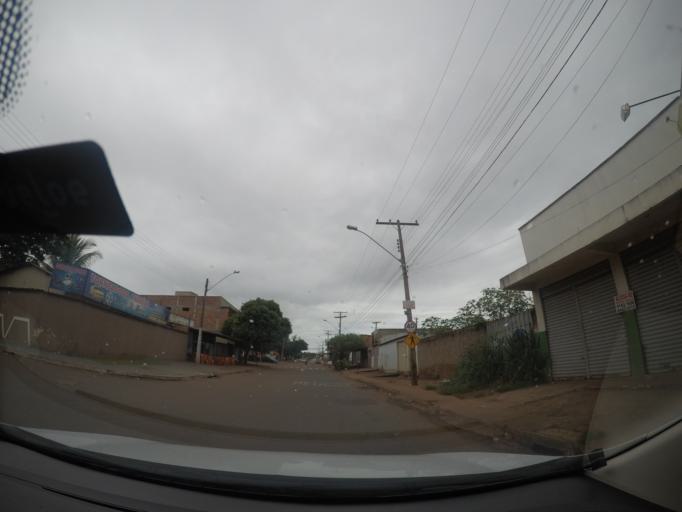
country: BR
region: Goias
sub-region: Goiania
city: Goiania
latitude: -16.6159
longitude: -49.3557
